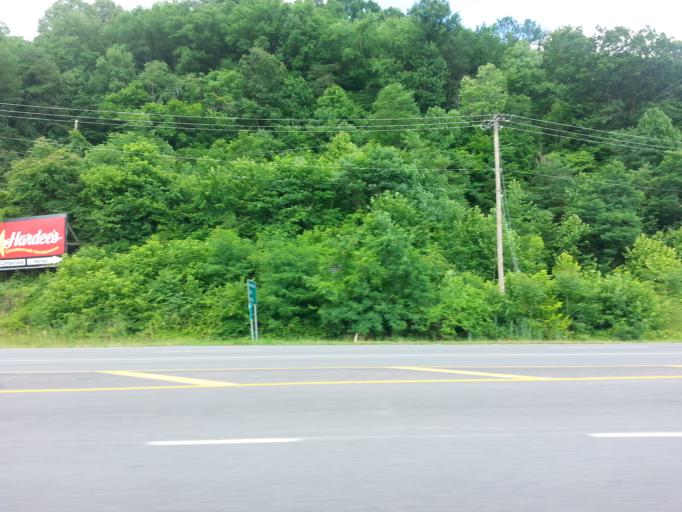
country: US
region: Kentucky
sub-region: Harlan County
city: Harlan
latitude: 36.8601
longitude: -83.3246
